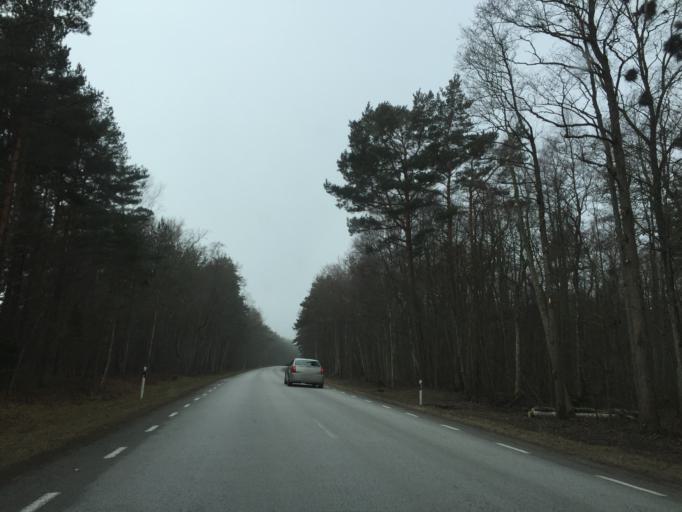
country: EE
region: Saare
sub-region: Kuressaare linn
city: Kuressaare
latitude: 58.2068
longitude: 22.3013
